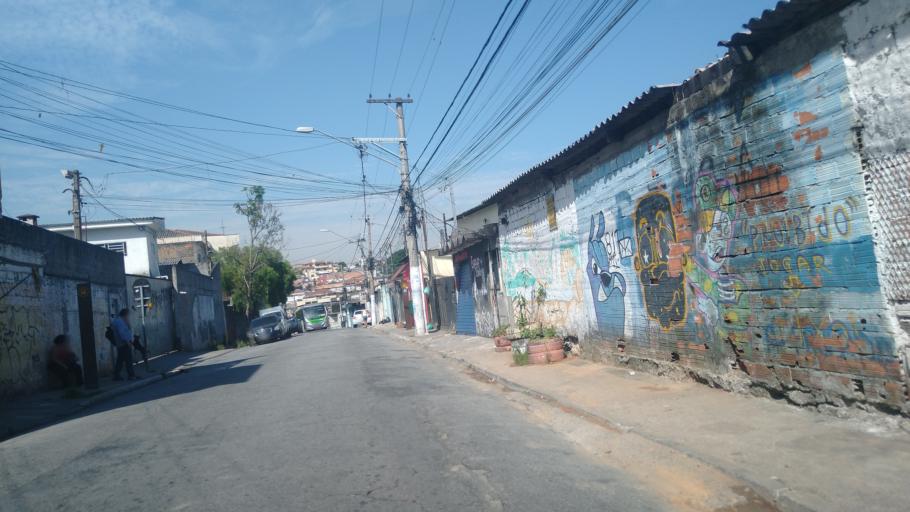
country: BR
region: Sao Paulo
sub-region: Sao Paulo
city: Sao Paulo
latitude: -23.4924
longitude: -46.6704
